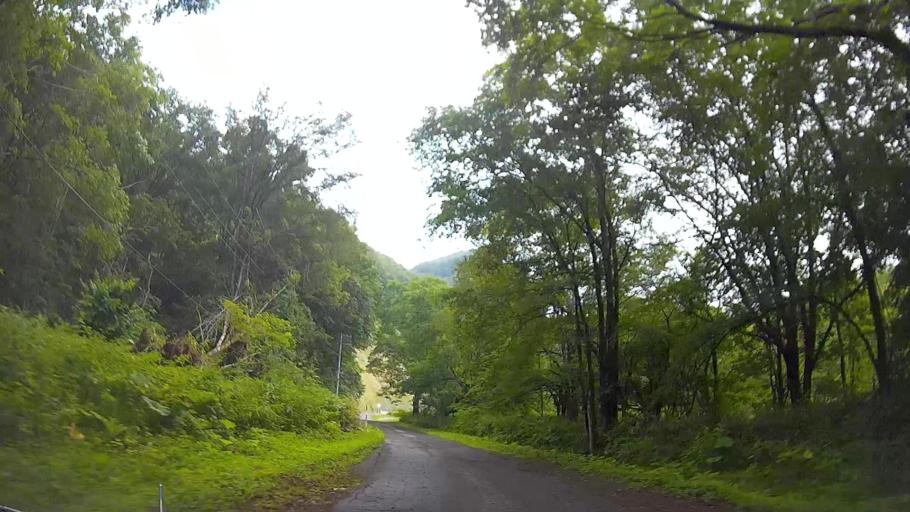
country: JP
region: Hokkaido
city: Nanae
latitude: 42.0741
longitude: 140.5228
